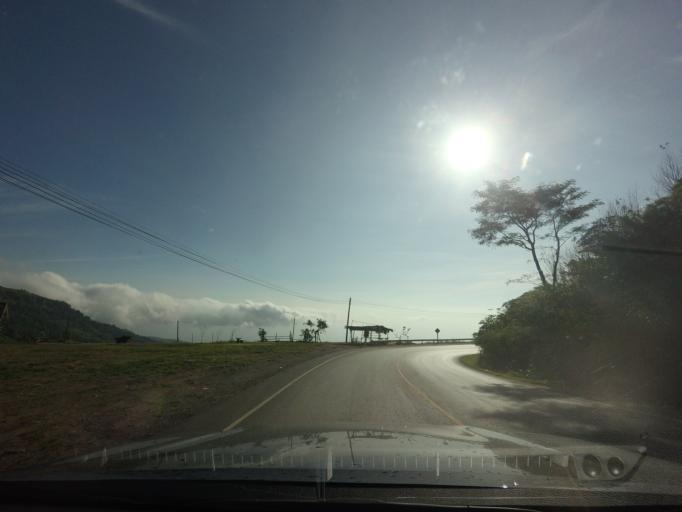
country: TH
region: Phetchabun
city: Lom Kao
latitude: 16.8817
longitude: 101.1021
